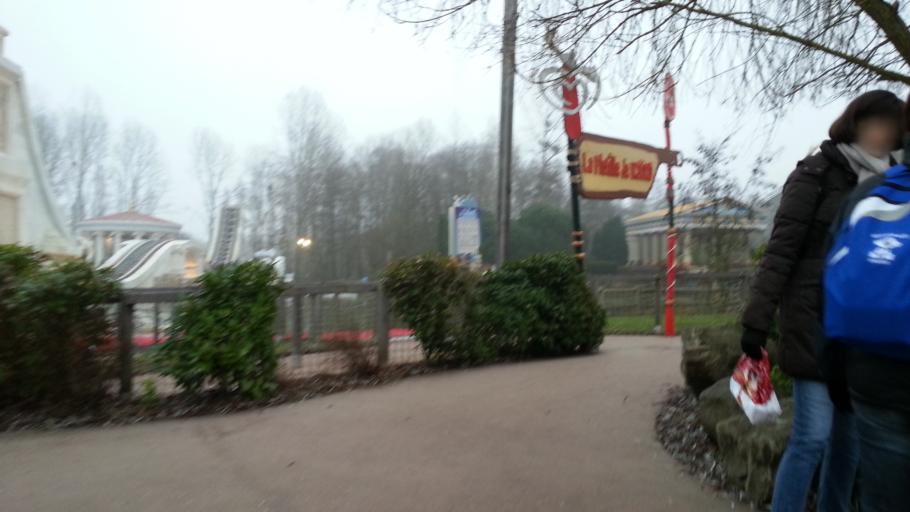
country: FR
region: Picardie
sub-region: Departement de l'Oise
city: Thiers-sur-Theve
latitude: 49.1318
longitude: 2.5724
